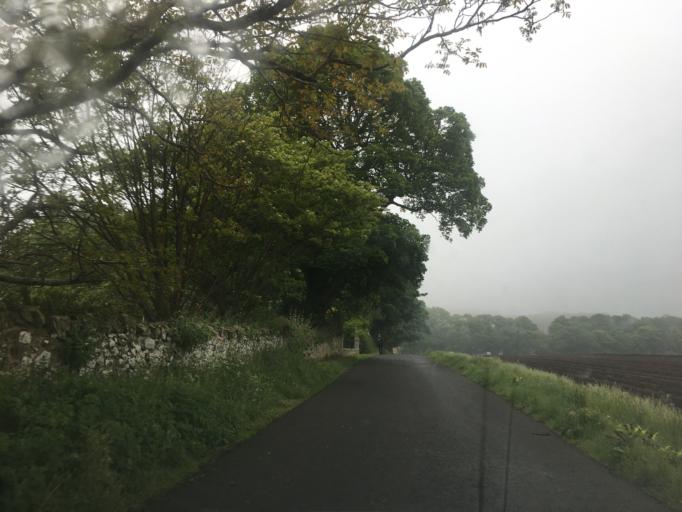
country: GB
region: Scotland
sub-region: Midlothian
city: Loanhead
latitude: 55.8966
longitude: -3.1927
